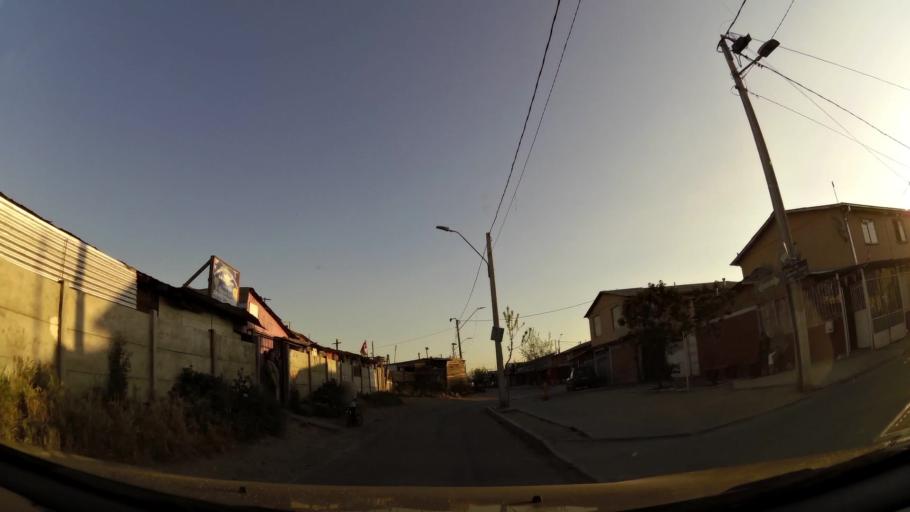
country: CL
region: Santiago Metropolitan
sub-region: Provincia de Maipo
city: San Bernardo
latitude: -33.5924
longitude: -70.6678
